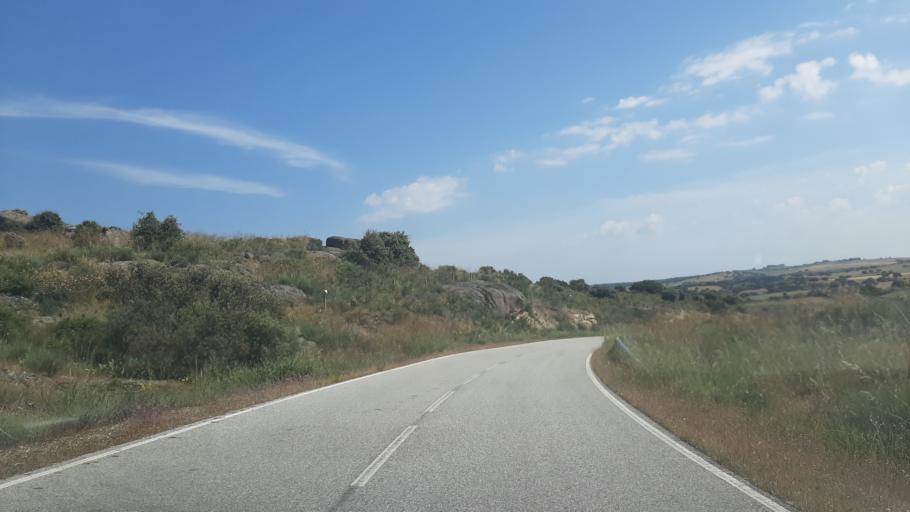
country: ES
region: Castille and Leon
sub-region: Provincia de Salamanca
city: Aldea del Obispo
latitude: 40.6474
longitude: -6.7826
